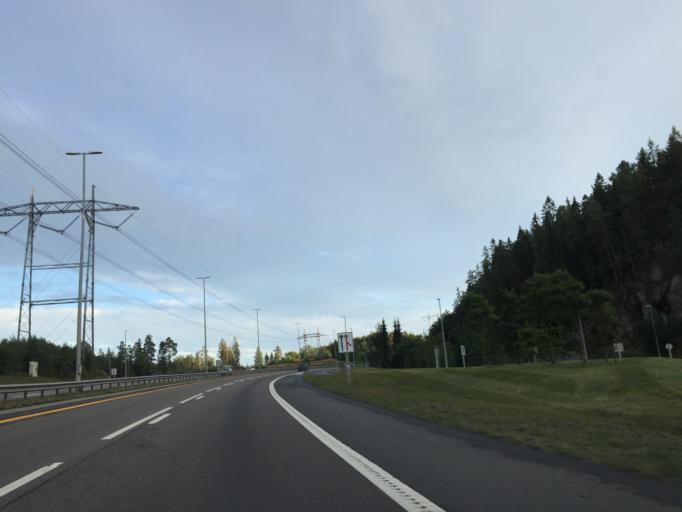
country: NO
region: Akershus
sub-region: Oppegard
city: Kolbotn
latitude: 59.8204
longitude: 10.8467
